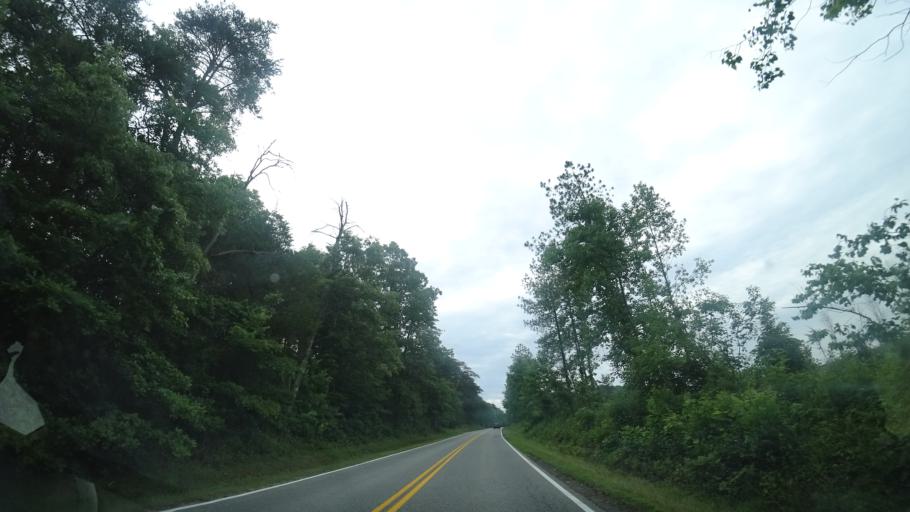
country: US
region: Virginia
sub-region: Spotsylvania County
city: Spotsylvania
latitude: 38.1378
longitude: -77.8000
